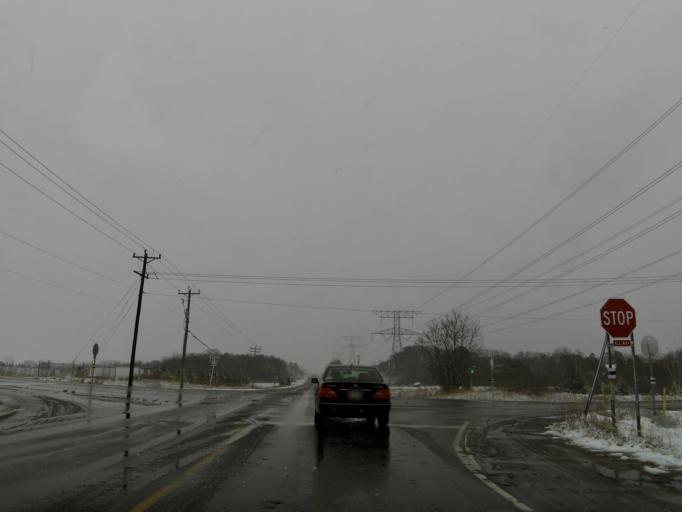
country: US
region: Minnesota
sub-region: Washington County
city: Lake Elmo
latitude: 44.9469
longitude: -92.8431
